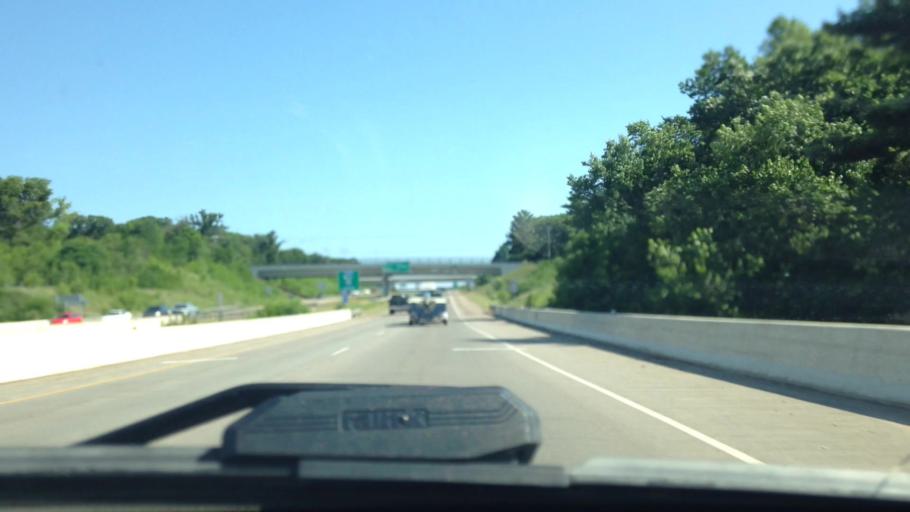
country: US
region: Wisconsin
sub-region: Eau Claire County
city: Altoona
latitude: 44.8238
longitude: -91.4538
